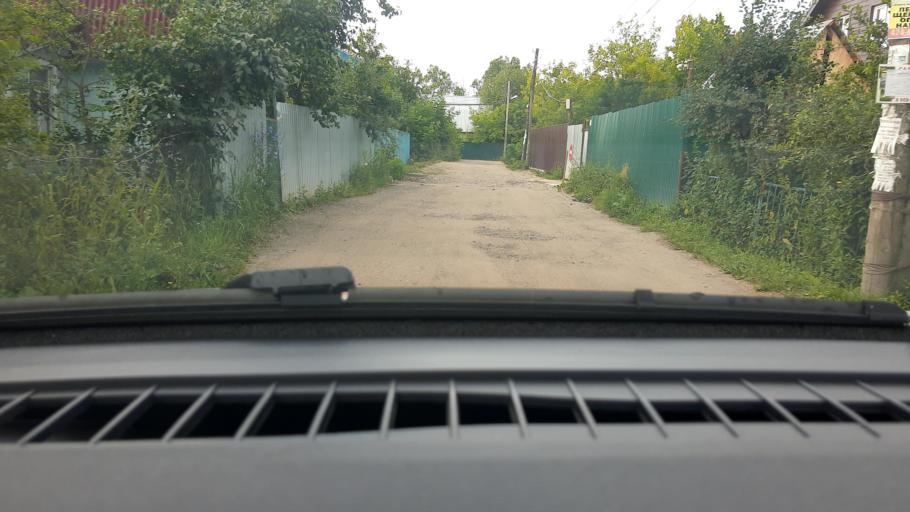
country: RU
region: Nizjnij Novgorod
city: Gorbatovka
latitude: 56.3137
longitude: 43.8307
